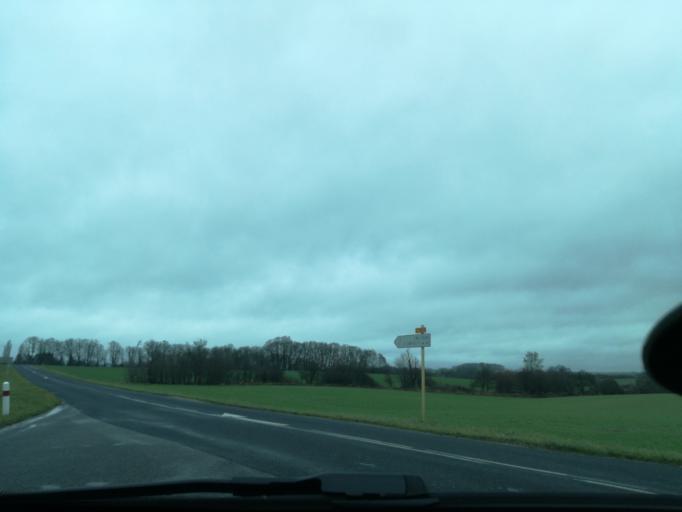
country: FR
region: Lorraine
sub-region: Departement de la Meuse
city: Clermont-en-Argonne
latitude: 49.0537
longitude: 5.1241
